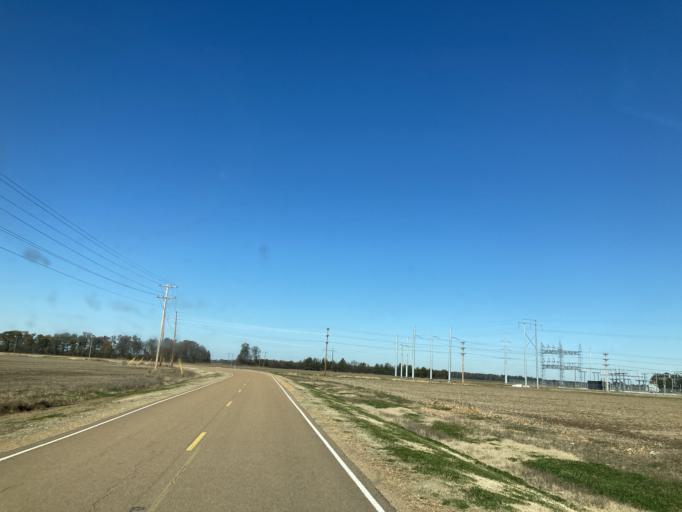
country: US
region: Mississippi
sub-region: Yazoo County
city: Yazoo City
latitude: 32.9139
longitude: -90.4467
